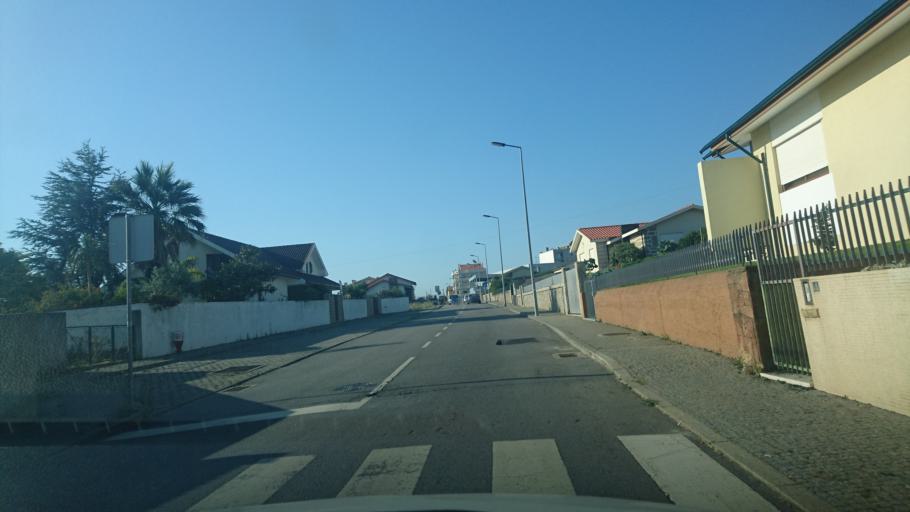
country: PT
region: Aveiro
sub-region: Ovar
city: Esmoriz
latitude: 40.9599
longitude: -8.6296
